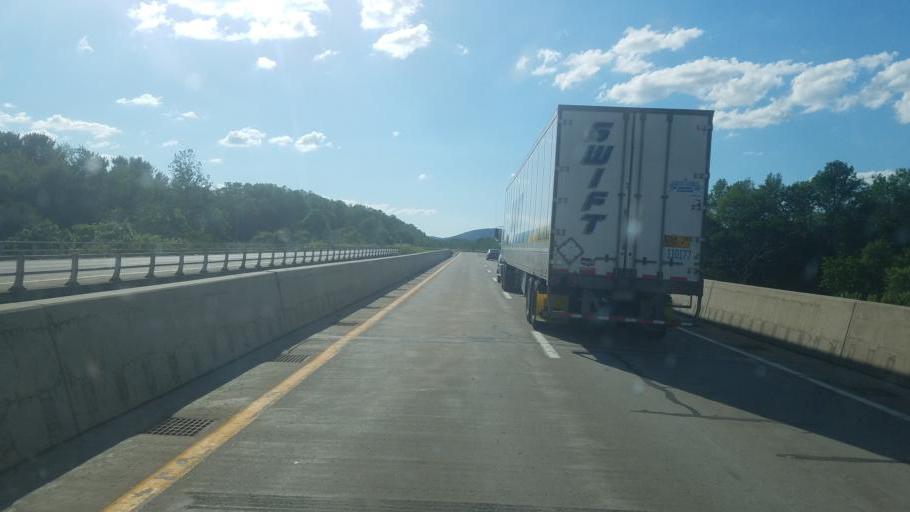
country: US
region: New York
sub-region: Cattaraugus County
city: Randolph
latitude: 42.1004
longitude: -78.8615
